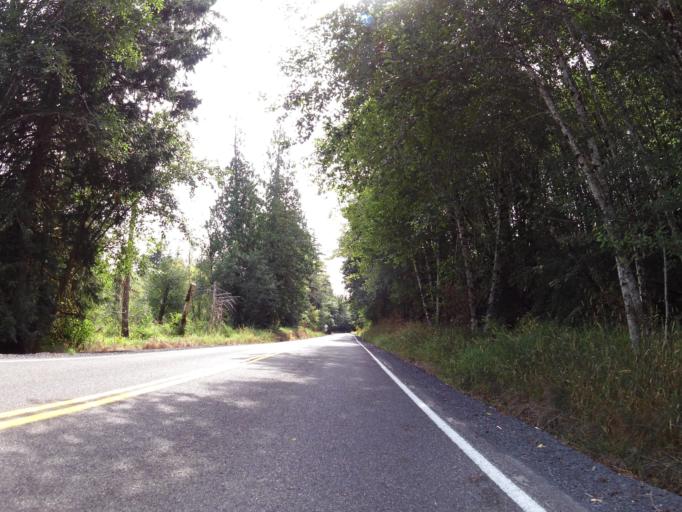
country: US
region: Washington
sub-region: Lewis County
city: Napavine
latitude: 46.5496
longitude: -122.9552
